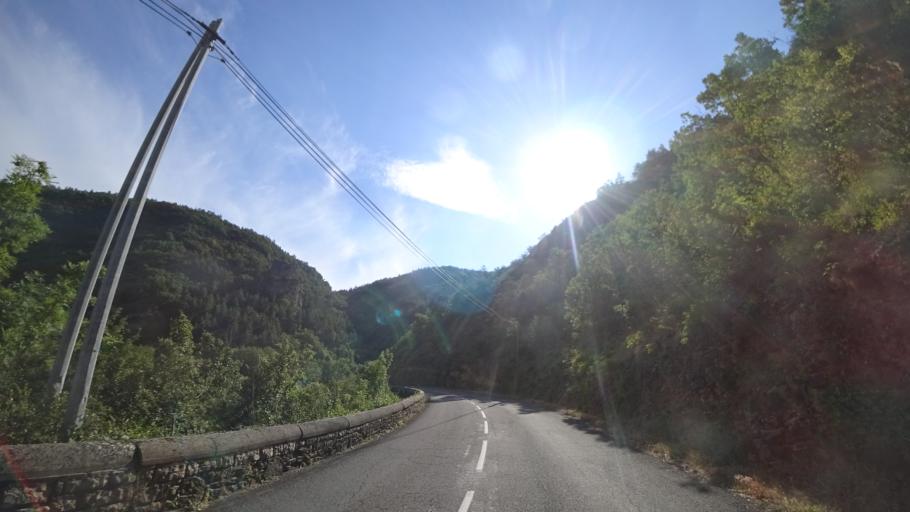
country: FR
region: Languedoc-Roussillon
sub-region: Departement de la Lozere
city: La Canourgue
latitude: 44.4085
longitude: 3.2438
